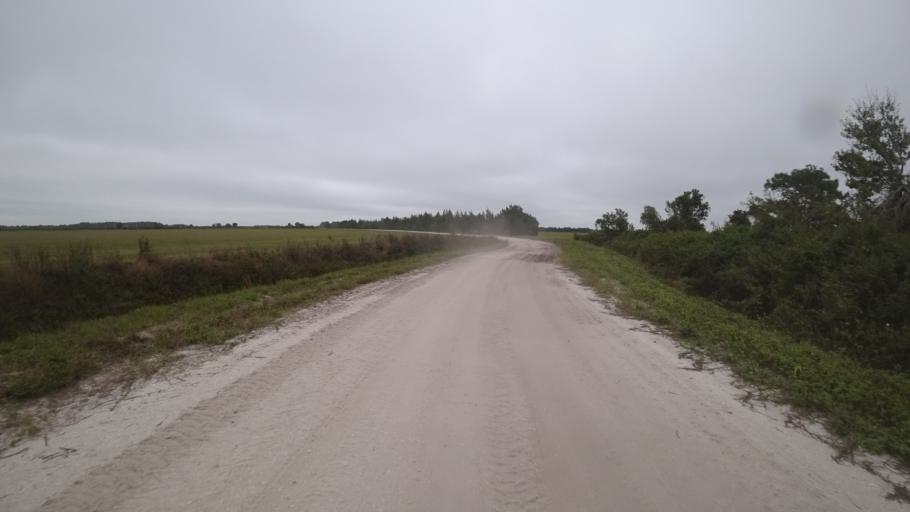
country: US
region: Florida
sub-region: Sarasota County
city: Warm Mineral Springs
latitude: 27.2954
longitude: -82.1350
